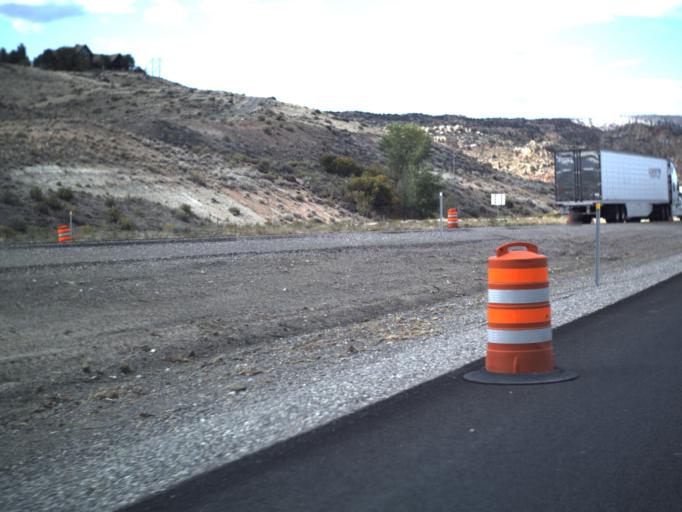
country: US
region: Utah
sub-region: Sevier County
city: Richfield
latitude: 38.7530
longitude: -112.1047
